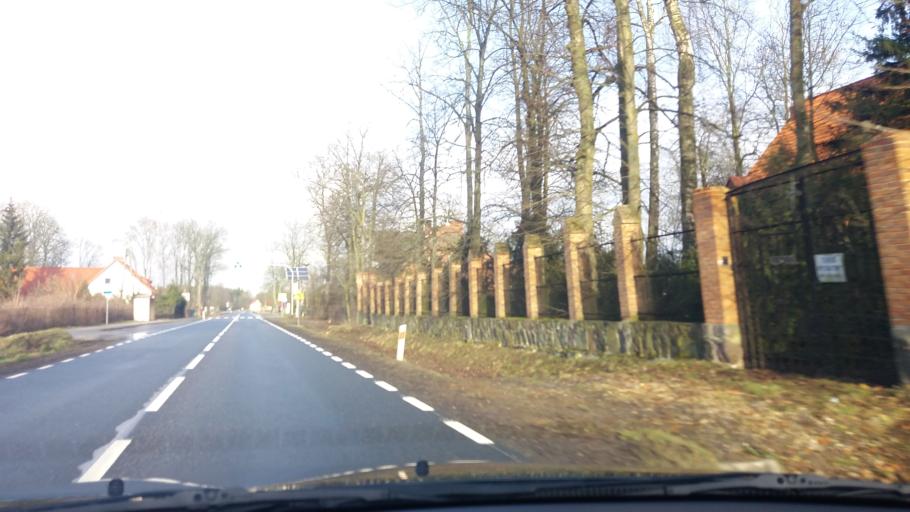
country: PL
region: Masovian Voivodeship
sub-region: Powiat przasnyski
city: Chorzele
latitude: 53.2892
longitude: 20.9125
